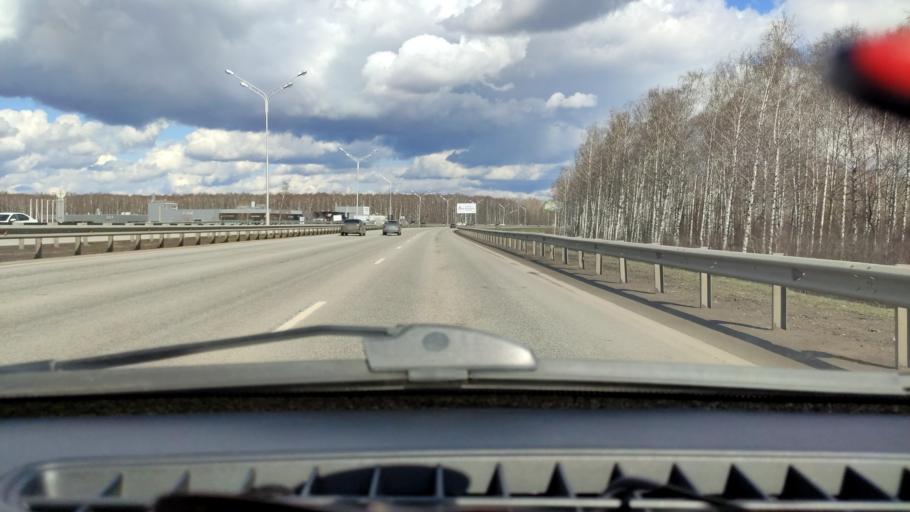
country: RU
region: Bashkortostan
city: Ufa
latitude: 54.6786
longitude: 55.9347
